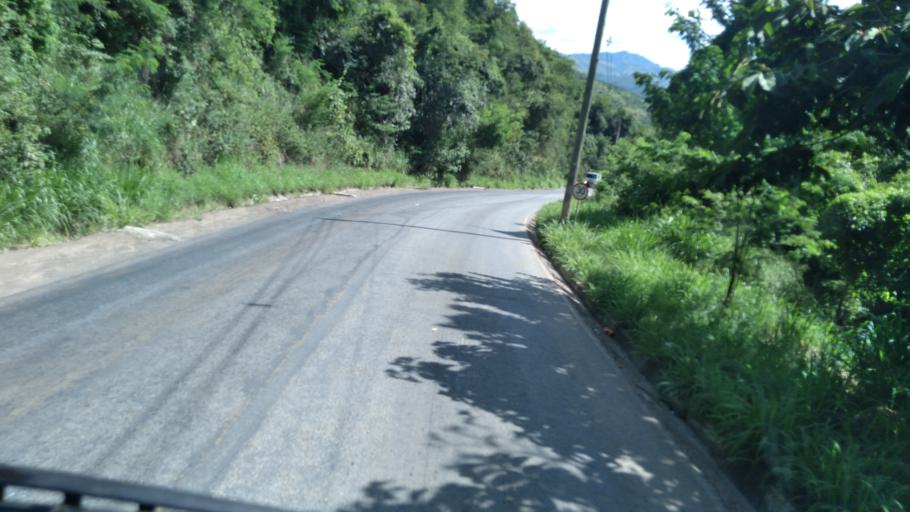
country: BR
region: Minas Gerais
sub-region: Santa Luzia
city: Santa Luzia
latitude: -19.8596
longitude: -43.8500
